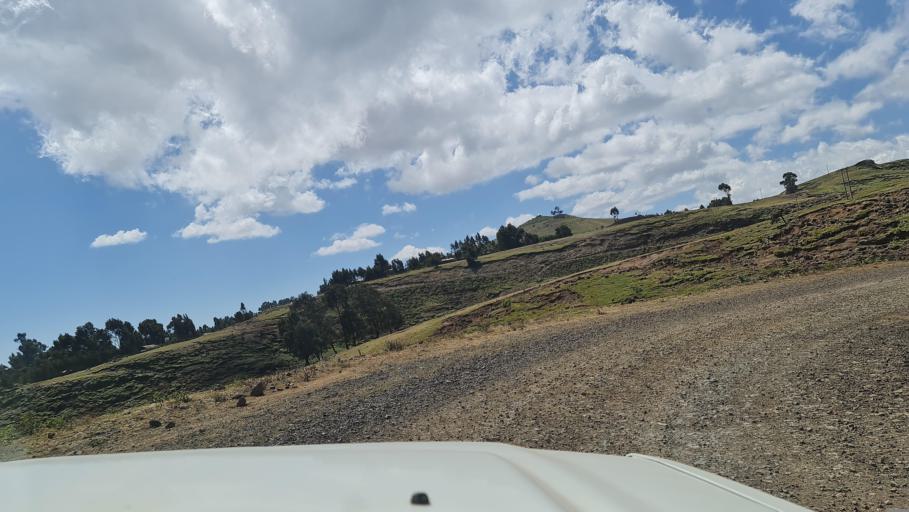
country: ET
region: Amhara
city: Debark'
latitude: 13.2167
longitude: 38.0099
